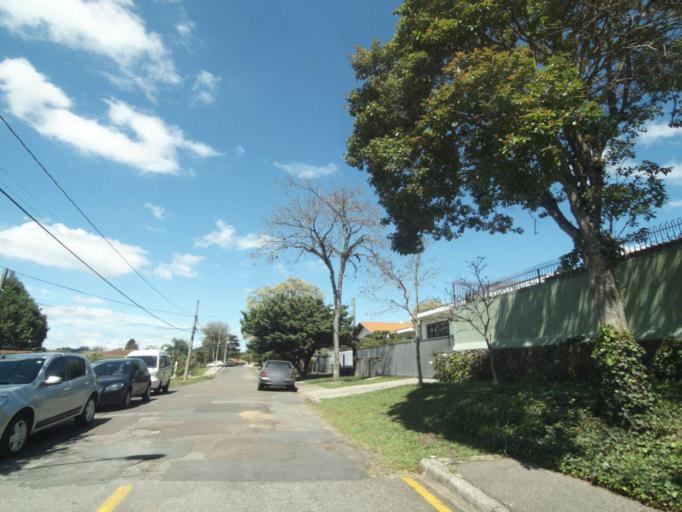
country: BR
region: Parana
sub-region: Curitiba
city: Curitiba
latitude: -25.3997
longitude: -49.2739
